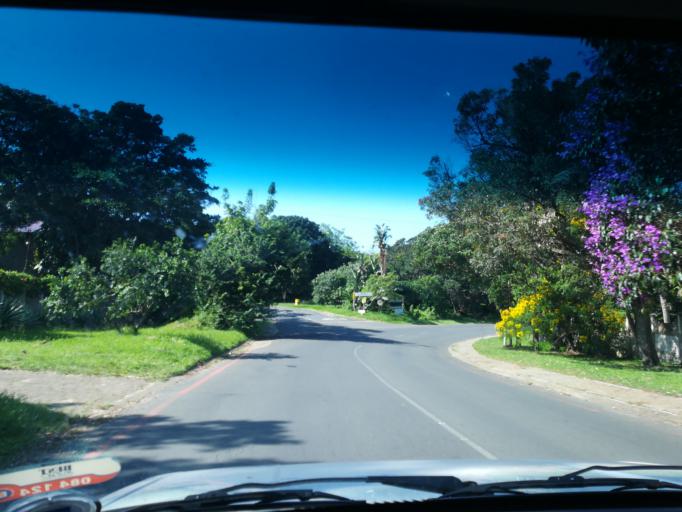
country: ZA
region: KwaZulu-Natal
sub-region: Ugu District Municipality
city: Scottburgh
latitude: -30.3823
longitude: 30.6914
